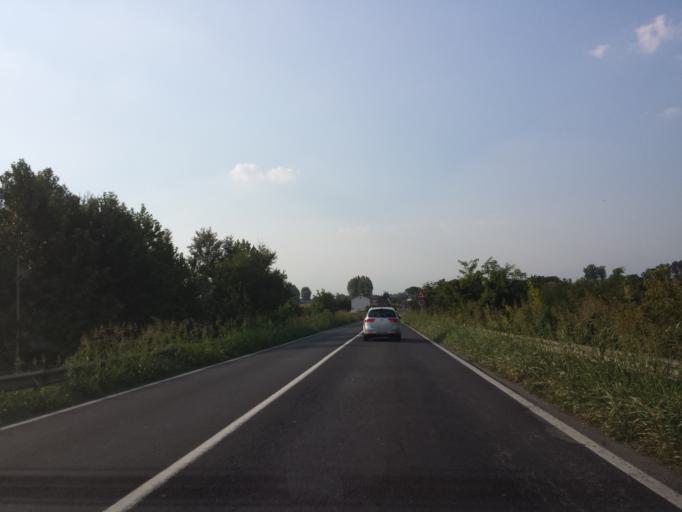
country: IT
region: Veneto
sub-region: Provincia di Vicenza
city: Grisignano di Zocco
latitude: 45.4839
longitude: 11.6801
